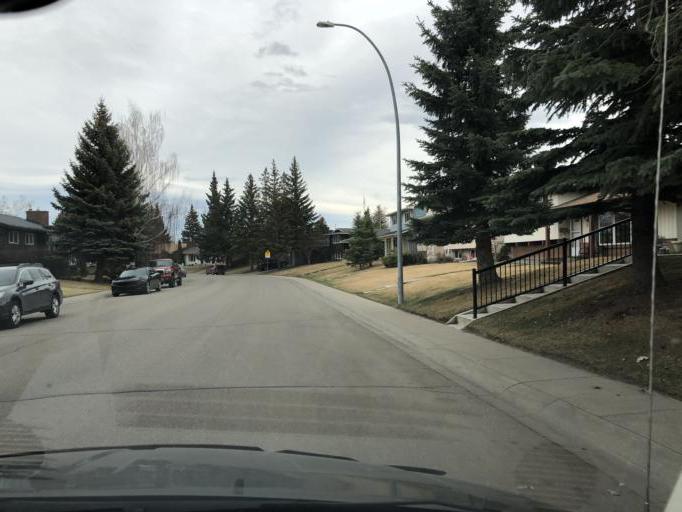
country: CA
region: Alberta
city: Calgary
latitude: 50.9323
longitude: -114.0427
